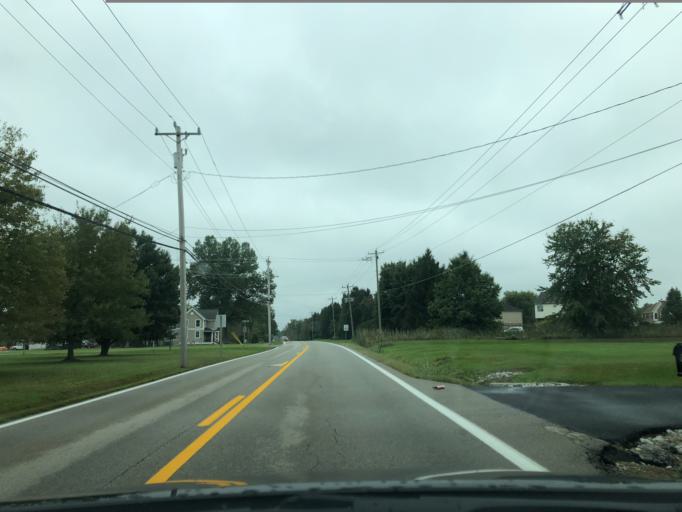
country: US
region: Ohio
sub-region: Hamilton County
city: Loveland
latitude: 39.2540
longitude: -84.2337
